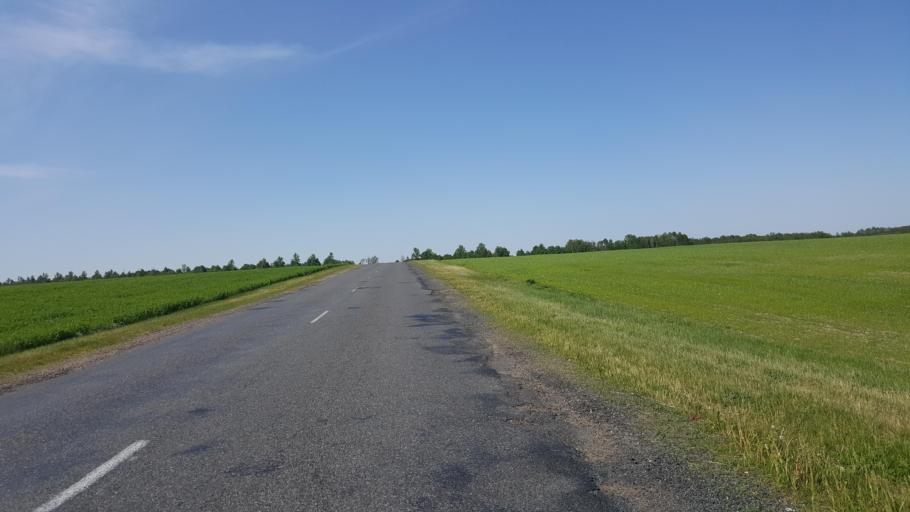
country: BY
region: Brest
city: Charnawchytsy
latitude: 52.3045
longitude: 23.6069
